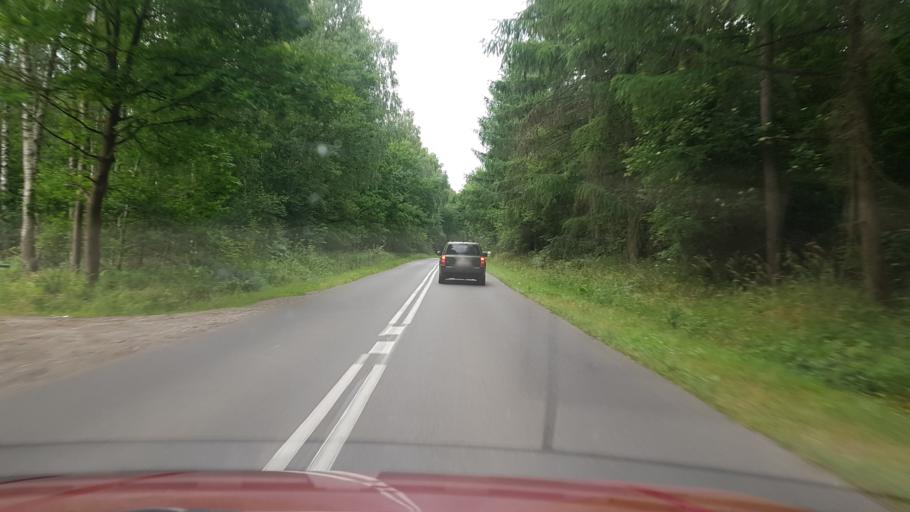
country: PL
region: West Pomeranian Voivodeship
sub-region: Powiat gryficki
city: Gryfice
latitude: 53.8858
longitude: 15.1586
